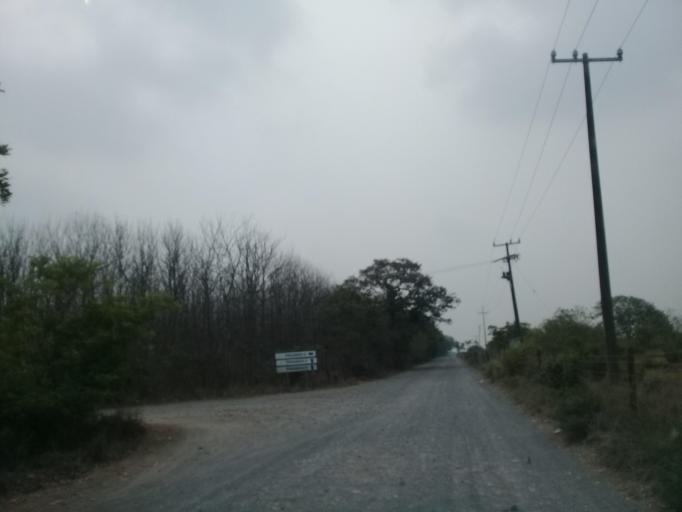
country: MX
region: Veracruz
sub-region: Medellin
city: La Laguna y Monte del Castillo
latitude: 18.9037
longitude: -96.1780
